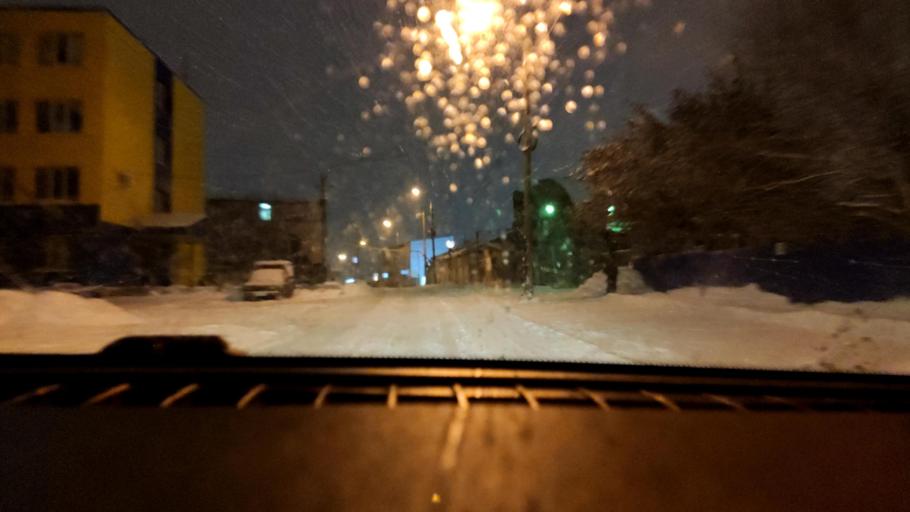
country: RU
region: Samara
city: Samara
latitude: 53.1878
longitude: 50.1510
